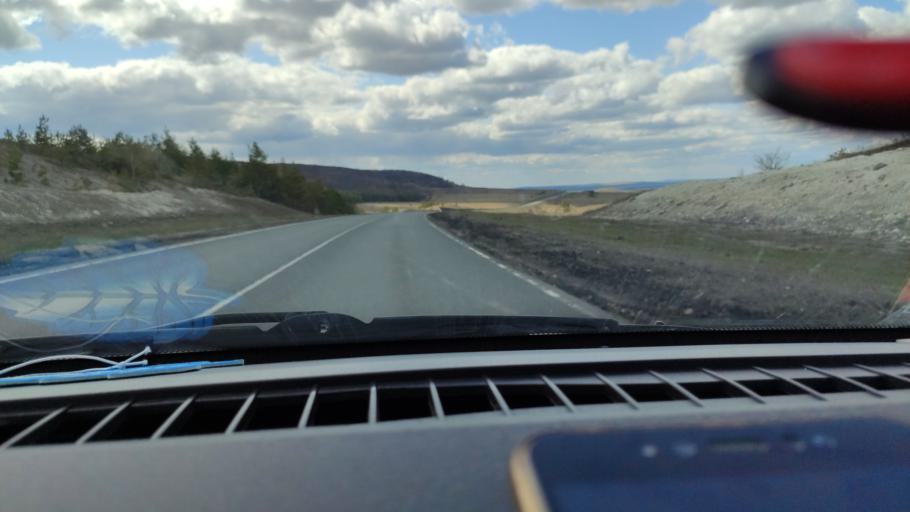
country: RU
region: Saratov
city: Alekseyevka
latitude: 52.3661
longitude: 47.9619
